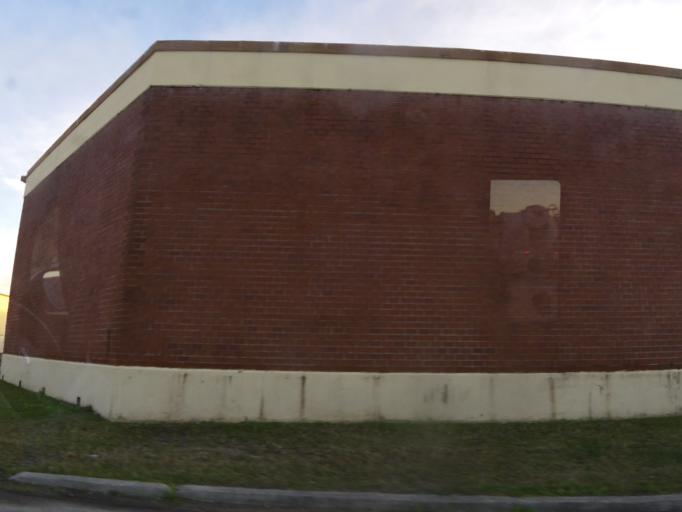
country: US
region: Florida
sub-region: Duval County
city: Jacksonville
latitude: 30.3478
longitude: -81.7114
